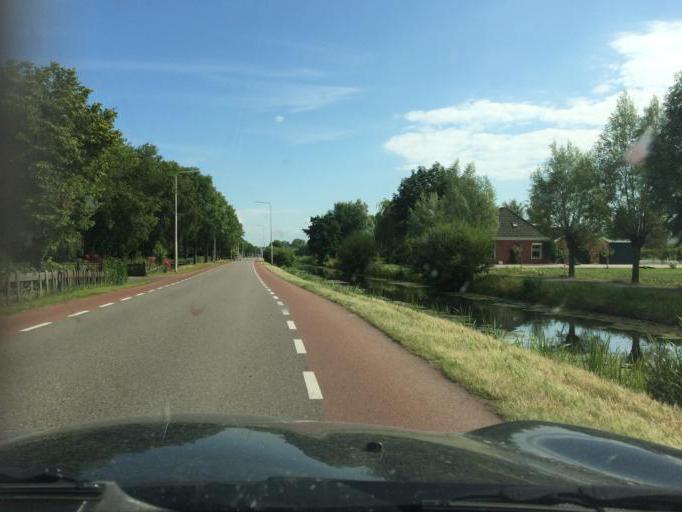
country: NL
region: Utrecht
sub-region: Gemeente Woerden
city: Woerden
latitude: 52.1050
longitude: 4.8944
